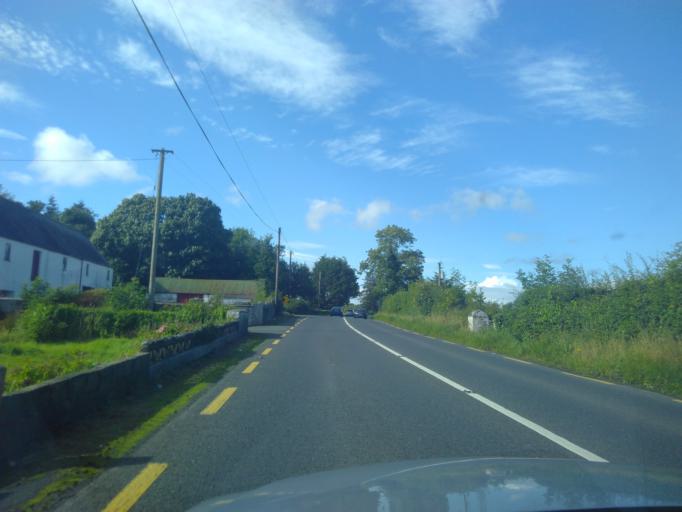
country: IE
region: Ulster
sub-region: County Donegal
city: Ballybofey
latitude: 54.8303
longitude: -7.7473
